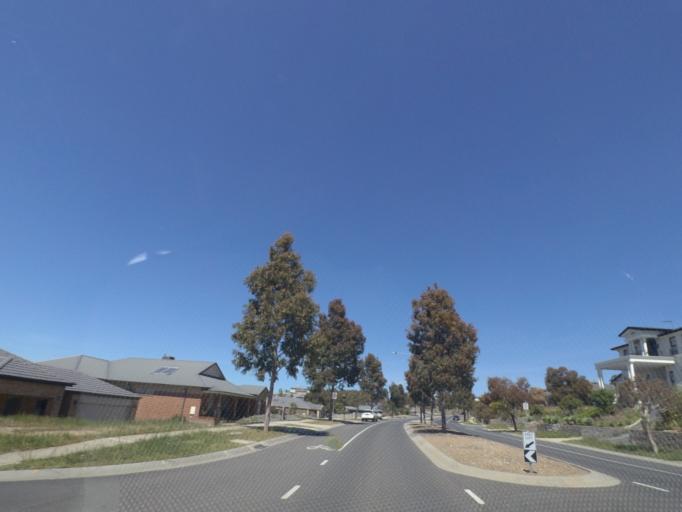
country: AU
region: Victoria
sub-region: Hume
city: Sunbury
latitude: -37.5655
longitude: 144.6982
